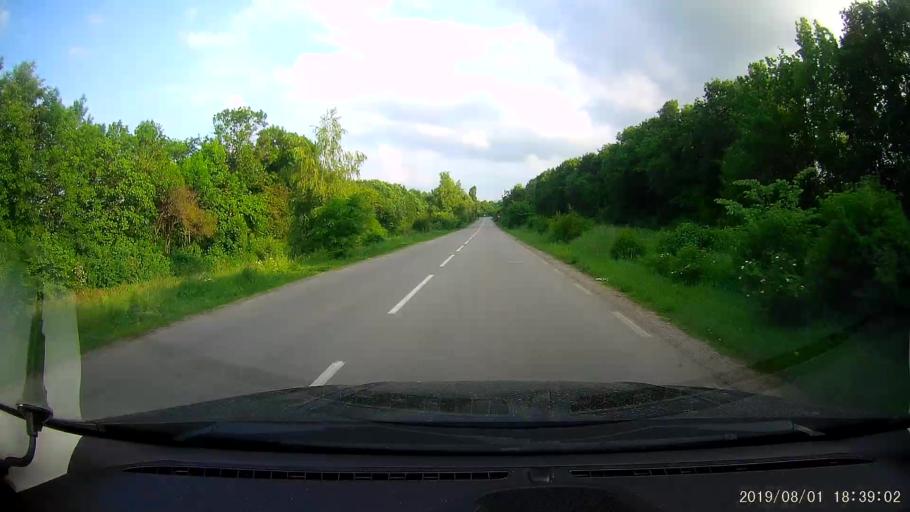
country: BG
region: Shumen
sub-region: Obshtina Khitrino
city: Gara Khitrino
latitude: 43.3939
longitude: 26.9173
